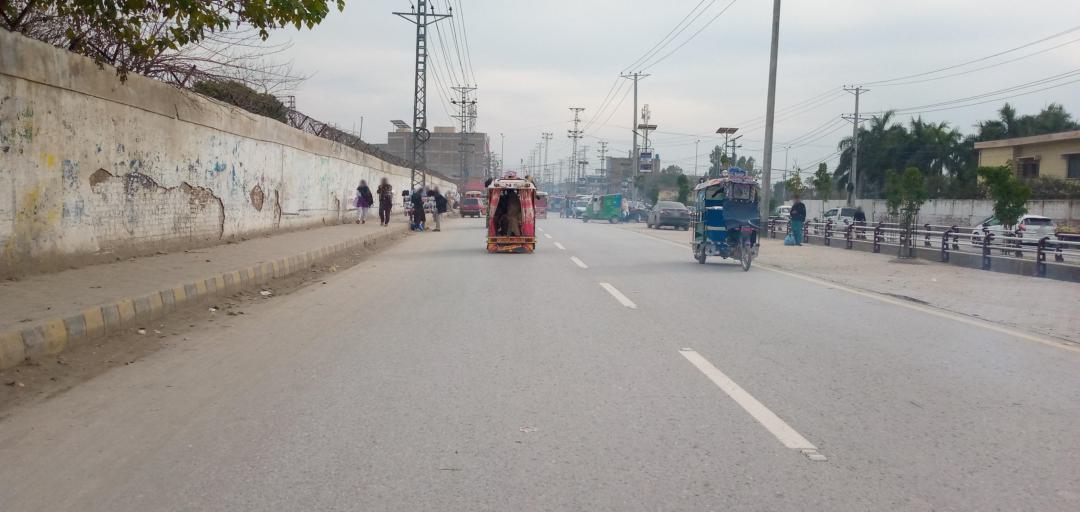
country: PK
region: Khyber Pakhtunkhwa
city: Peshawar
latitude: 33.9993
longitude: 71.4693
